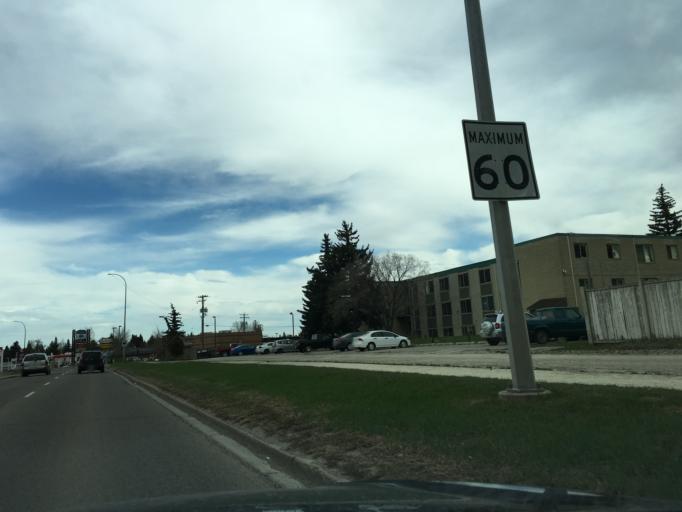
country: CA
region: Alberta
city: Calgary
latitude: 50.9643
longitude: -114.0620
